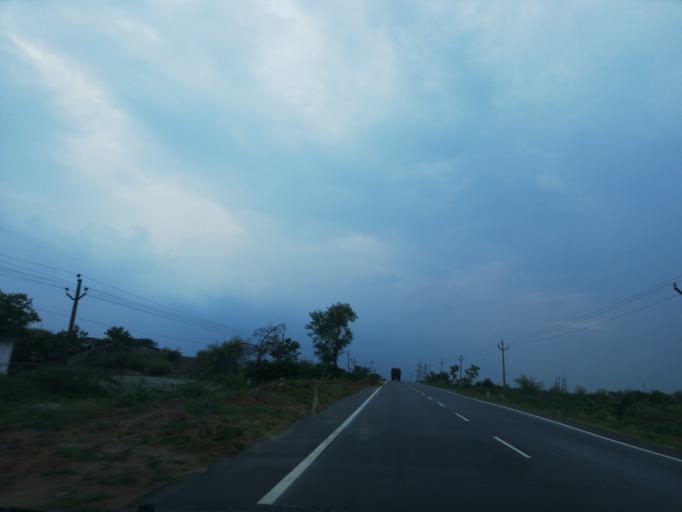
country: IN
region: Andhra Pradesh
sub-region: Guntur
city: Macherla
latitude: 16.6729
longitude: 79.2753
